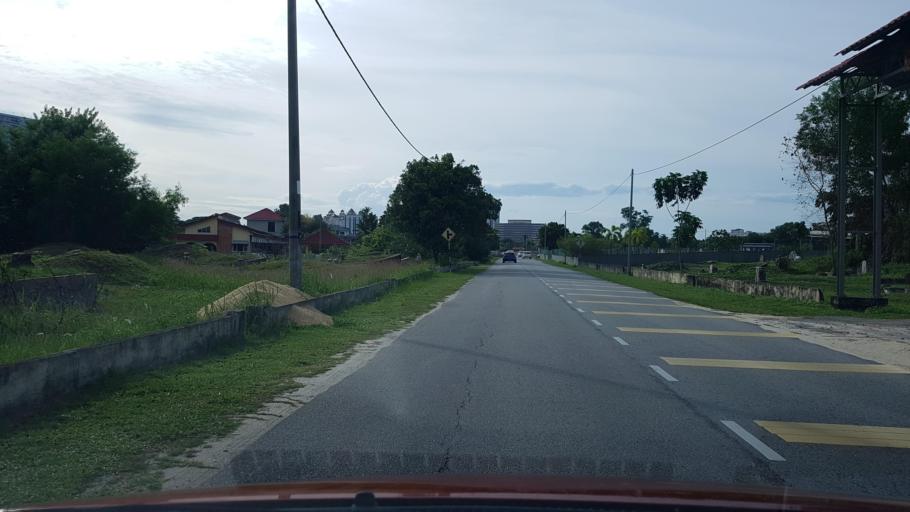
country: MY
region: Terengganu
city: Kuala Terengganu
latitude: 5.3196
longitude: 103.1472
